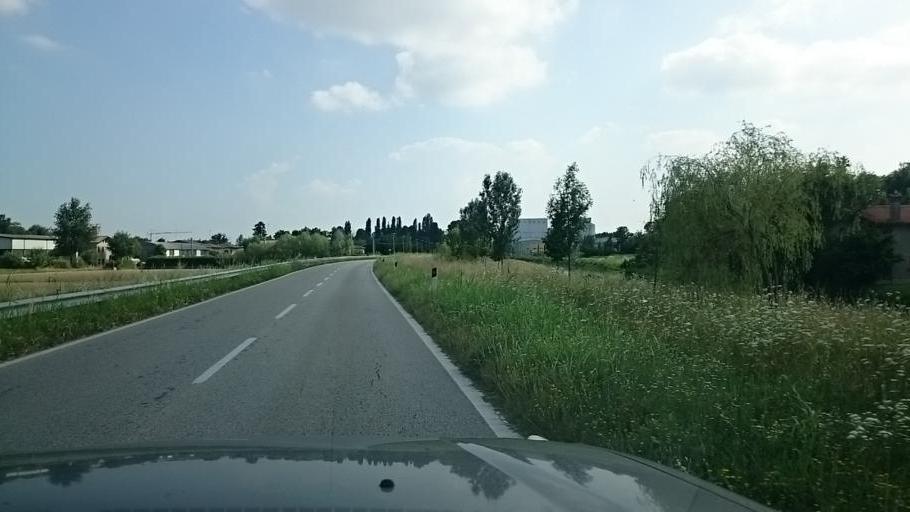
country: IT
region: Veneto
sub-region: Provincia di Padova
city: Santa Maria di Non
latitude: 45.5206
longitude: 11.8669
